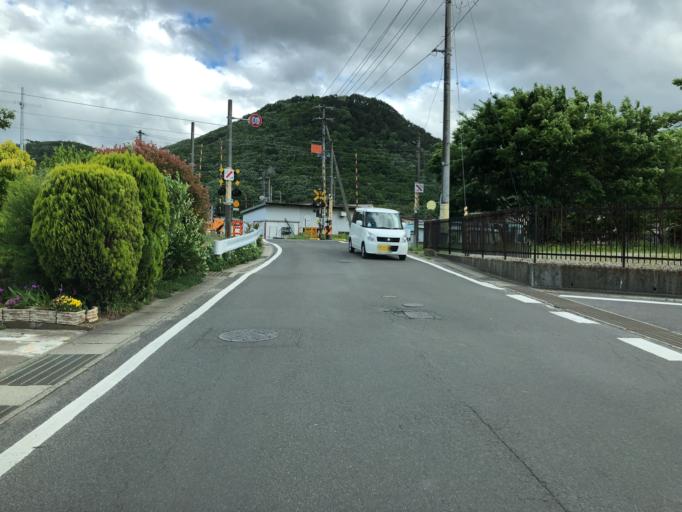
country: JP
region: Fukushima
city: Fukushima-shi
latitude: 37.7778
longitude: 140.4581
